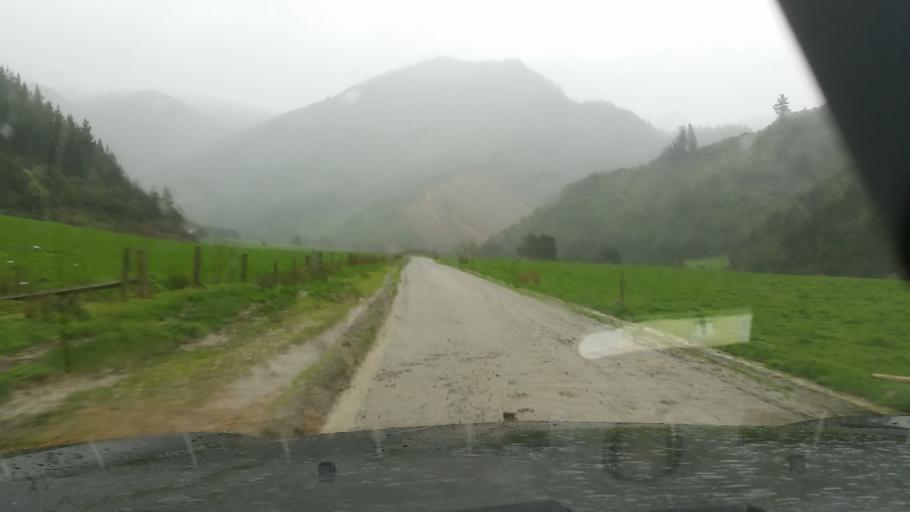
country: NZ
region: Marlborough
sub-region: Marlborough District
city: Picton
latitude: -41.3547
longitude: 173.9258
